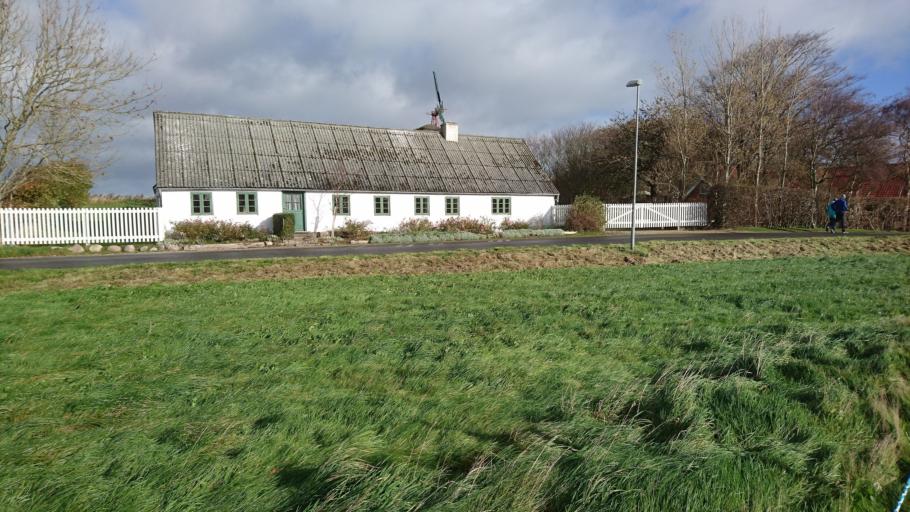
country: DK
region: North Denmark
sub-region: Morso Kommune
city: Nykobing Mors
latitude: 56.8166
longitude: 9.0203
